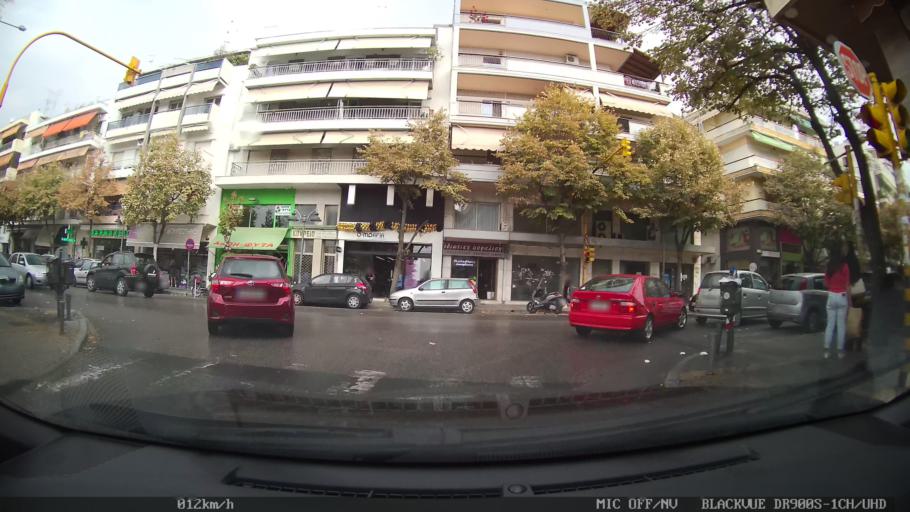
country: GR
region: Central Macedonia
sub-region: Nomos Thessalonikis
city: Triandria
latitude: 40.6129
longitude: 22.9814
